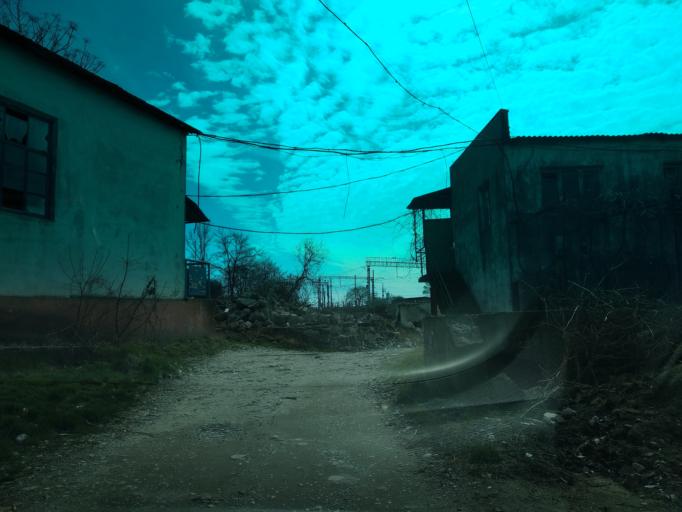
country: RU
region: Krasnodarskiy
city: Shepsi
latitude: 44.0335
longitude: 39.1435
